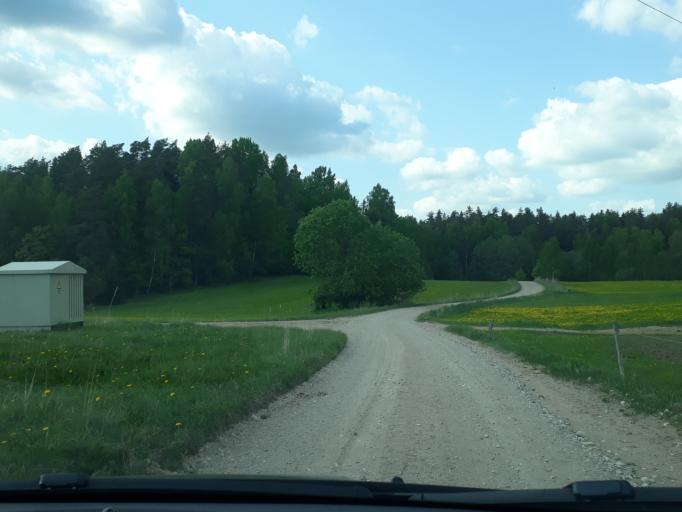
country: LV
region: Ligatne
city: Ligatne
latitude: 57.2663
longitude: 24.9857
